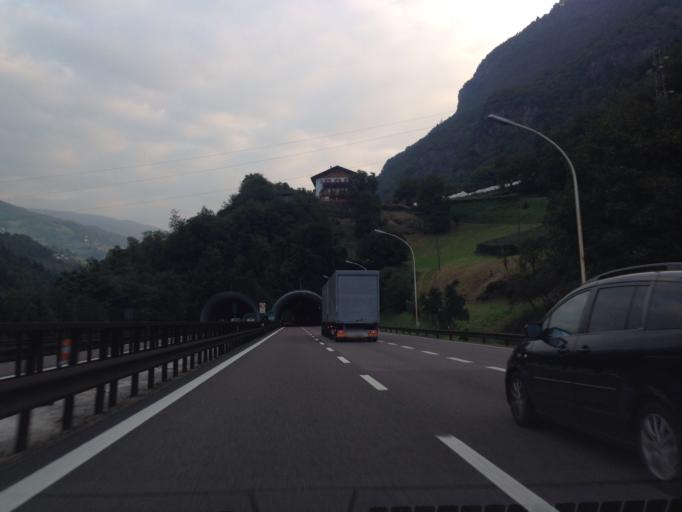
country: IT
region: Trentino-Alto Adige
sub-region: Bolzano
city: Ponte Gardena
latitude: 46.5709
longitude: 11.5229
